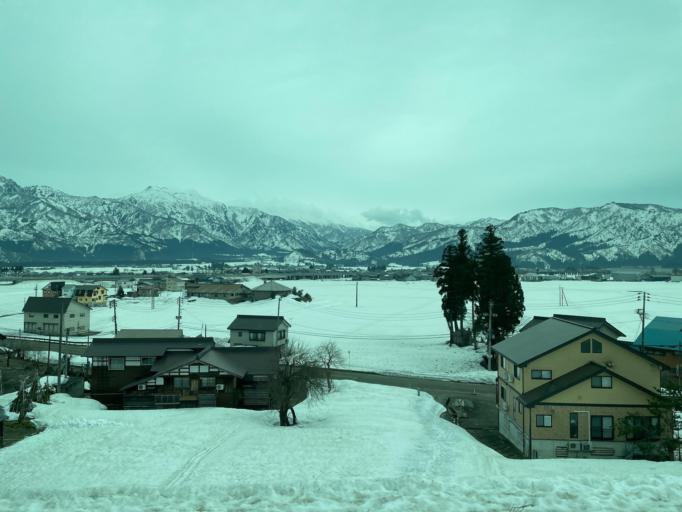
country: JP
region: Niigata
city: Shiozawa
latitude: 37.0318
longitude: 138.8336
